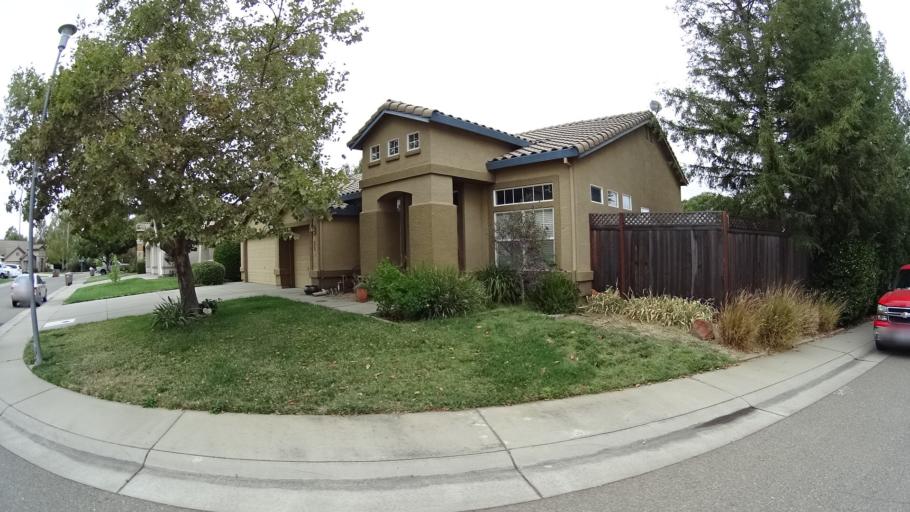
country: US
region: California
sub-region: Sacramento County
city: Laguna
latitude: 38.4168
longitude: -121.4527
